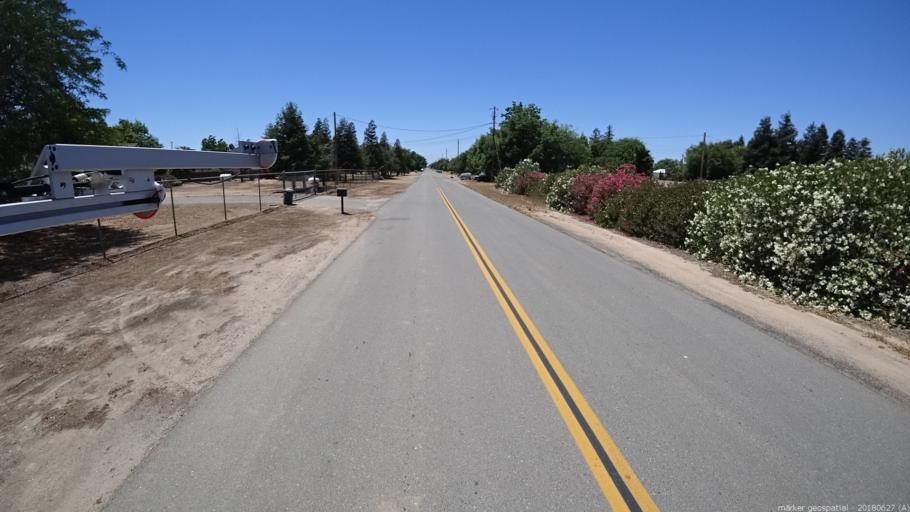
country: US
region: California
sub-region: Madera County
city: Bonadelle Ranchos-Madera Ranchos
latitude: 36.9353
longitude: -119.8853
